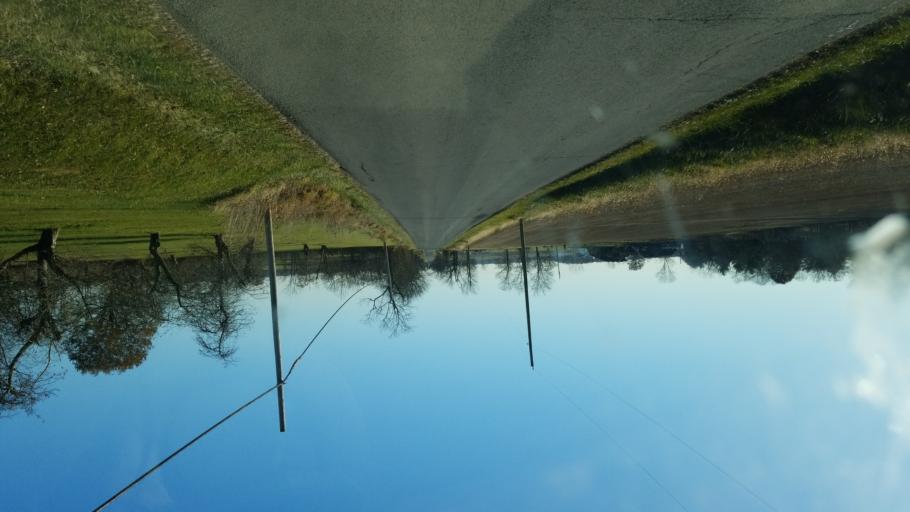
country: US
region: Ohio
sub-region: Morrow County
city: Cardington
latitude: 40.4670
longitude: -82.8921
